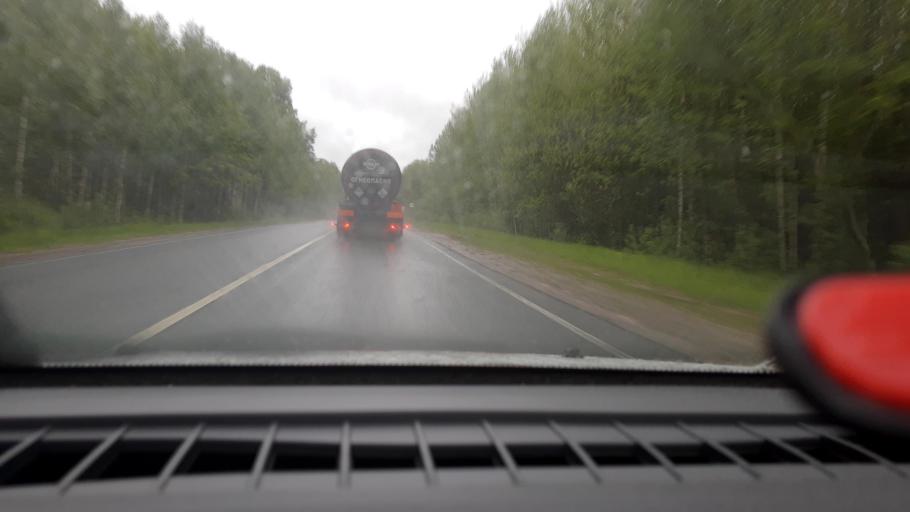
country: RU
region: Nizjnij Novgorod
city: Vladimirskoye
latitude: 56.8737
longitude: 44.9532
